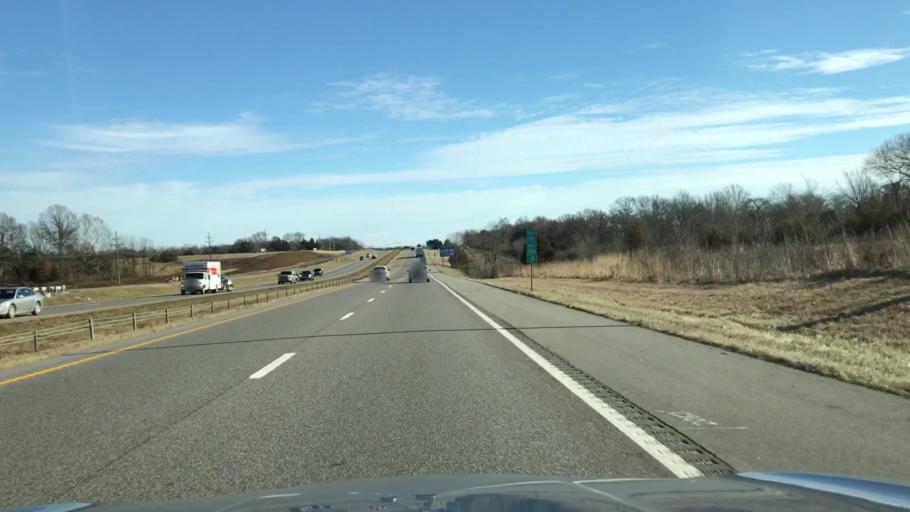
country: US
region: Missouri
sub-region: Saint Charles County
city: Wentzville
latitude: 38.8071
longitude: -90.9161
